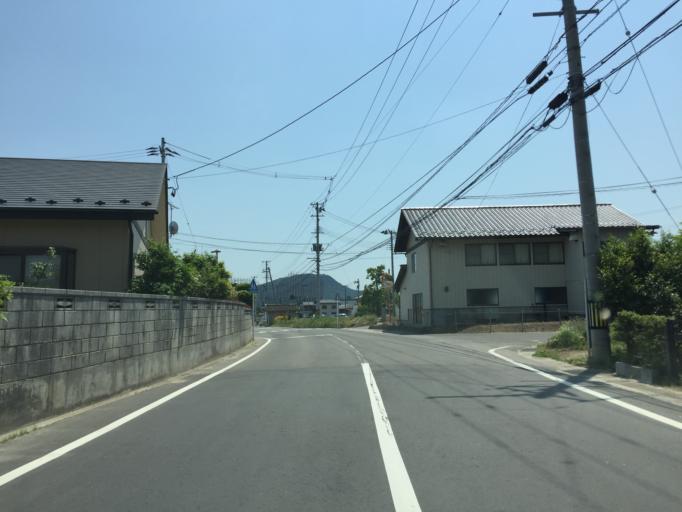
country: JP
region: Fukushima
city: Fukushima-shi
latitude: 37.7991
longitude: 140.4725
